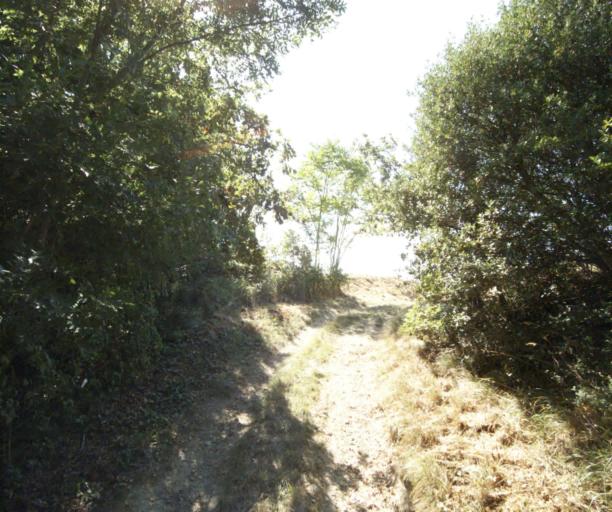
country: FR
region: Midi-Pyrenees
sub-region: Departement de la Haute-Garonne
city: Saint-Felix-Lauragais
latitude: 43.4749
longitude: 1.9146
